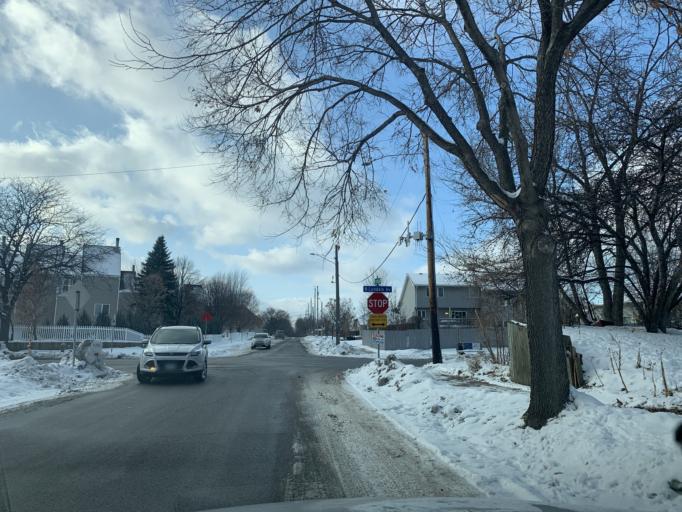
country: US
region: Minnesota
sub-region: Hennepin County
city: Minneapolis
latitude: 44.9931
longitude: -93.2876
